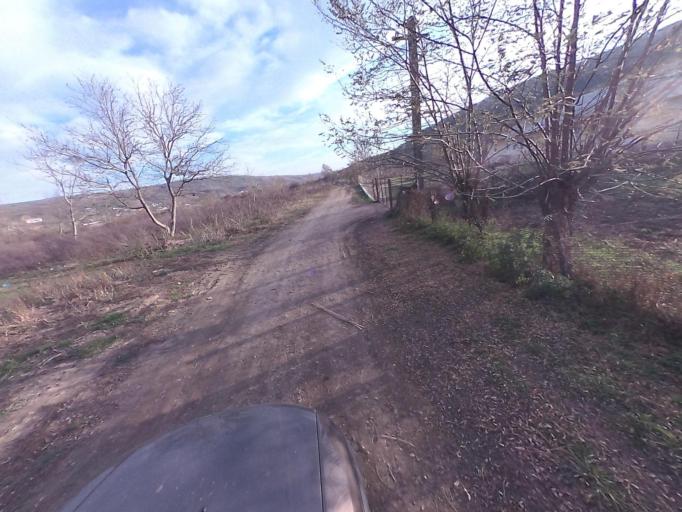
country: RO
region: Vaslui
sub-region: Comuna Gherghesti
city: Gherghesti
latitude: 46.4889
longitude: 27.5295
